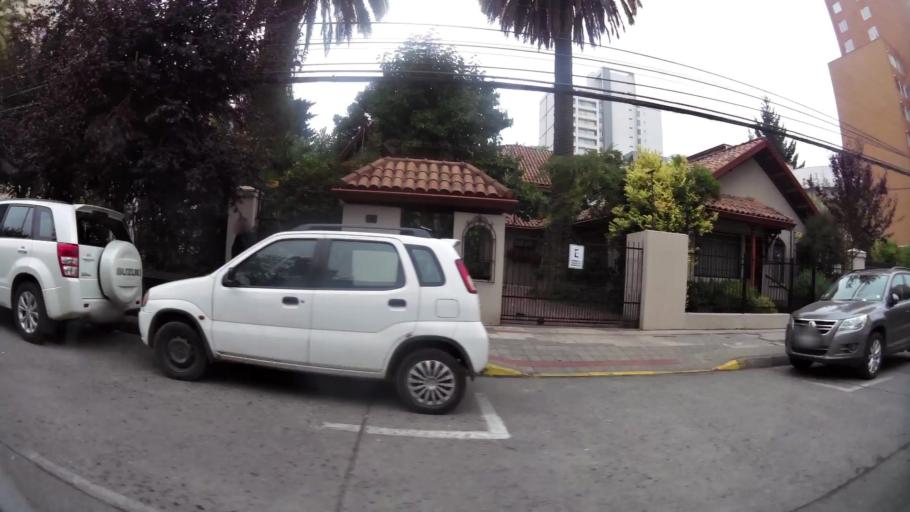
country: CL
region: Biobio
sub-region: Provincia de Concepcion
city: Concepcion
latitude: -36.8289
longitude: -73.0419
